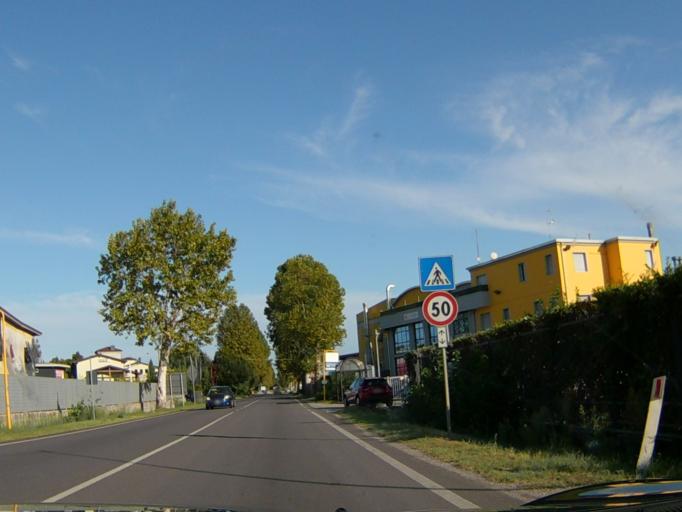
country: IT
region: Lombardy
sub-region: Provincia di Brescia
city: Ponte San Marco
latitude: 45.4783
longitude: 10.3924
